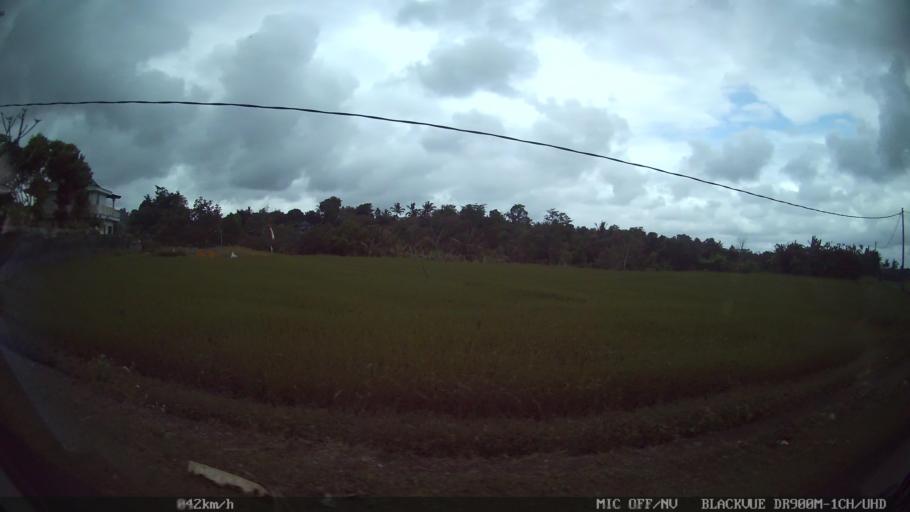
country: ID
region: Bali
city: Banjar Cemenggon
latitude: -8.5311
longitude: 115.1944
